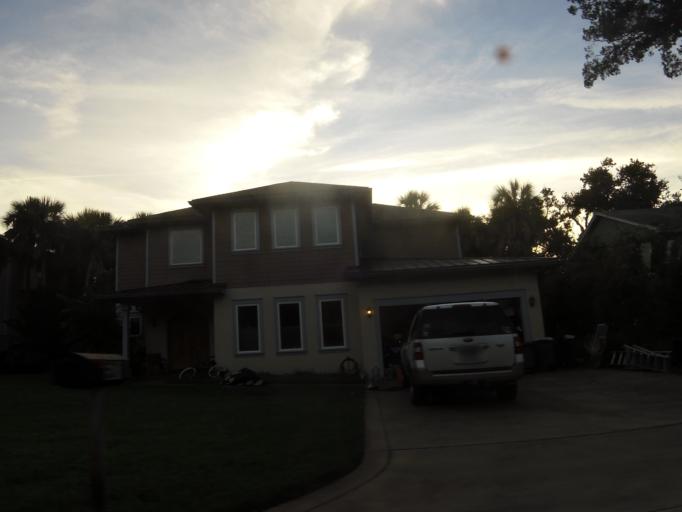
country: US
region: Florida
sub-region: Saint Johns County
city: Palm Valley
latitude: 30.1310
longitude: -81.3833
